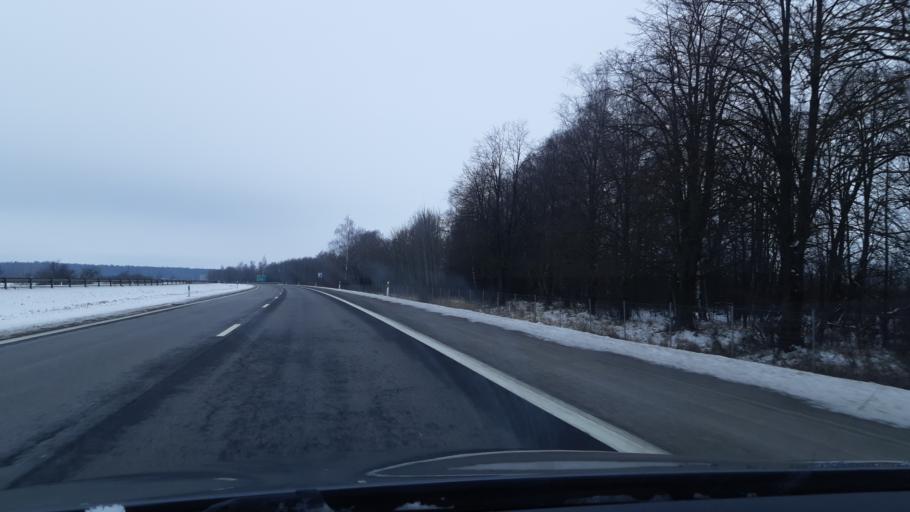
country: LT
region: Kauno apskritis
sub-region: Kaunas
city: Sargenai
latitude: 55.0882
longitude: 23.8108
